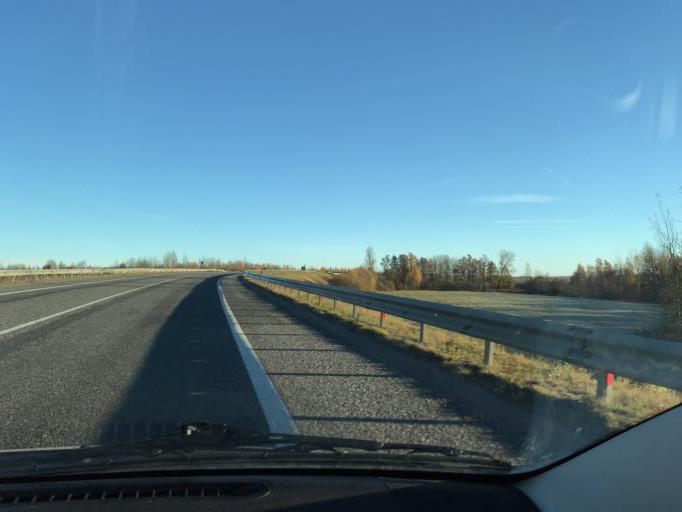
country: BY
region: Vitebsk
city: Vitebsk
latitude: 55.1035
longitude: 30.3013
